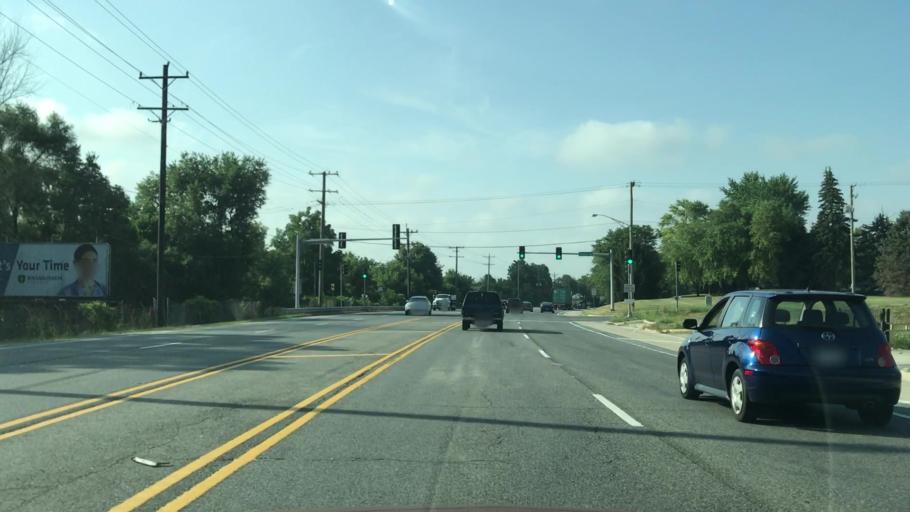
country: US
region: Illinois
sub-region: Will County
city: Lockport
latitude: 41.6117
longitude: -88.0753
